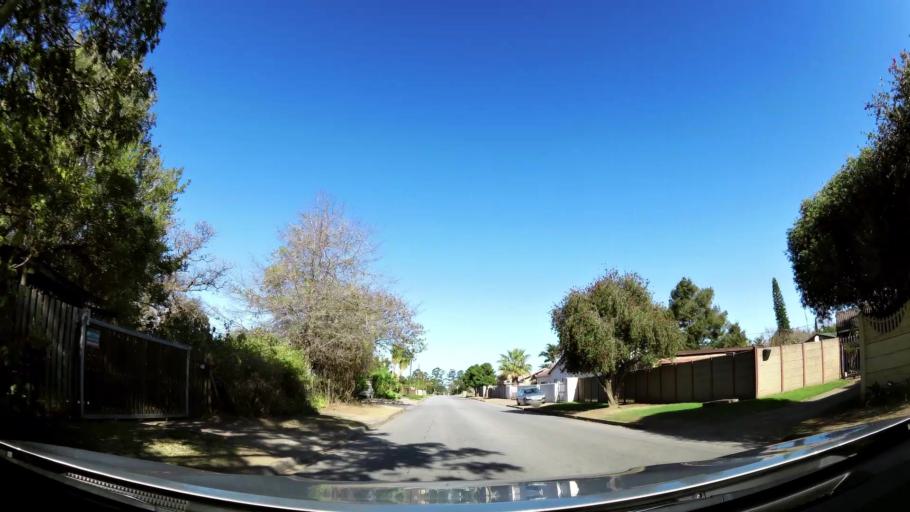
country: ZA
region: Western Cape
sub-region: Eden District Municipality
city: George
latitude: -33.9473
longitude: 22.4173
